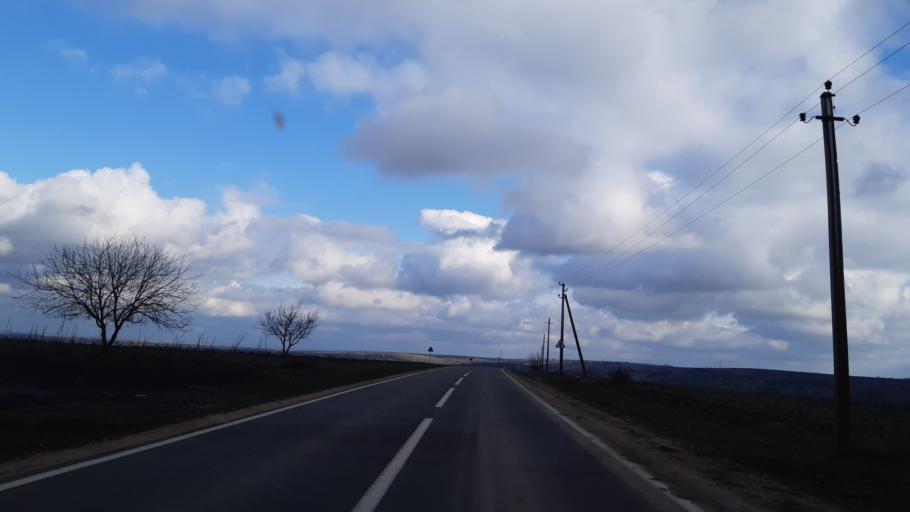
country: MD
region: Chisinau
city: Ciorescu
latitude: 47.2304
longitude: 28.9865
